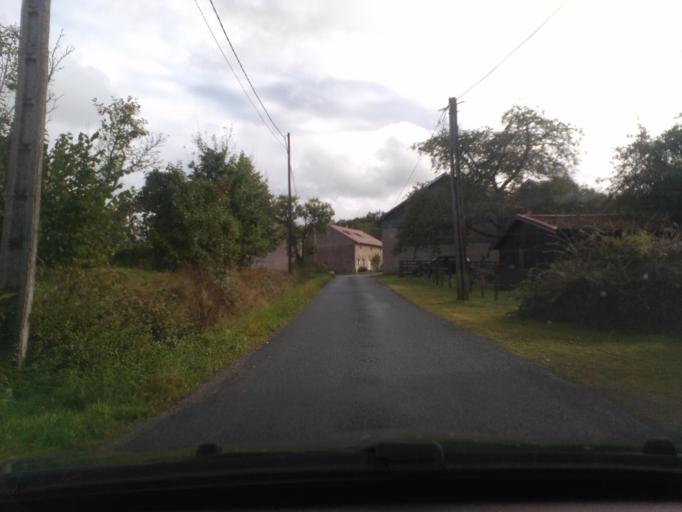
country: FR
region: Lorraine
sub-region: Departement des Vosges
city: Taintrux
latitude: 48.2311
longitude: 6.8936
